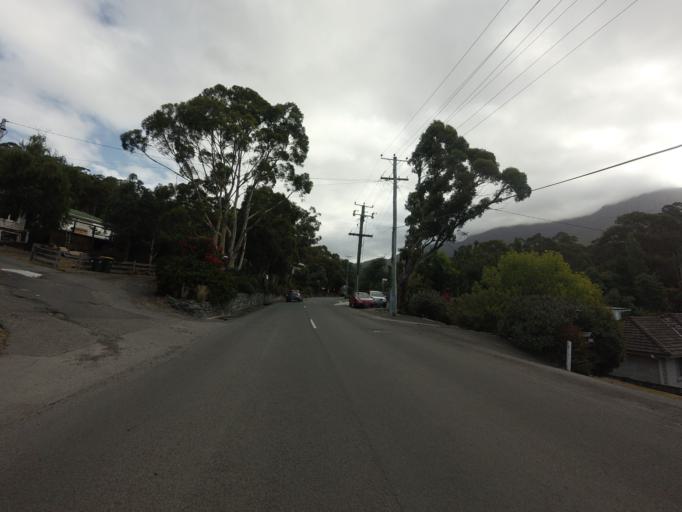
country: AU
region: Tasmania
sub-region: Hobart
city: Dynnyrne
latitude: -42.9012
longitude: 147.2812
